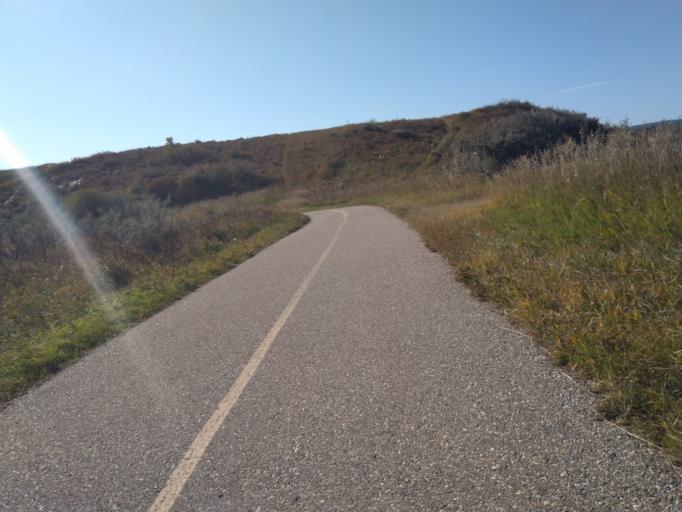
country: CA
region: Alberta
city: Calgary
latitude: 51.1325
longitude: -114.0488
